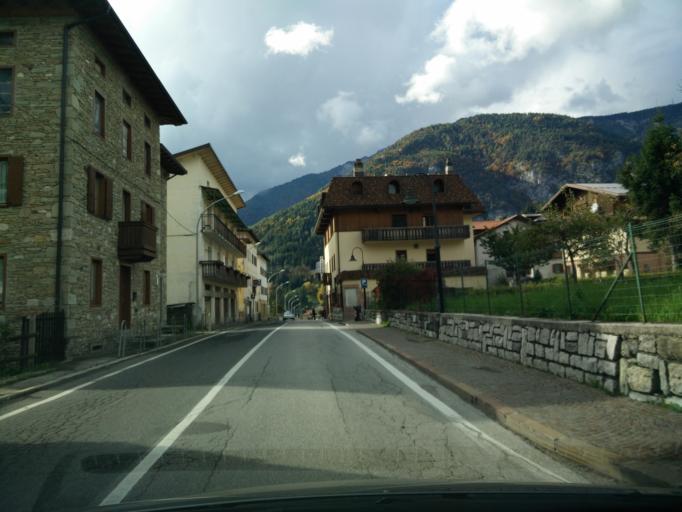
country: IT
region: Veneto
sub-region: Provincia di Belluno
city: Lorenzago di Cadore
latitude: 46.4889
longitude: 12.4620
